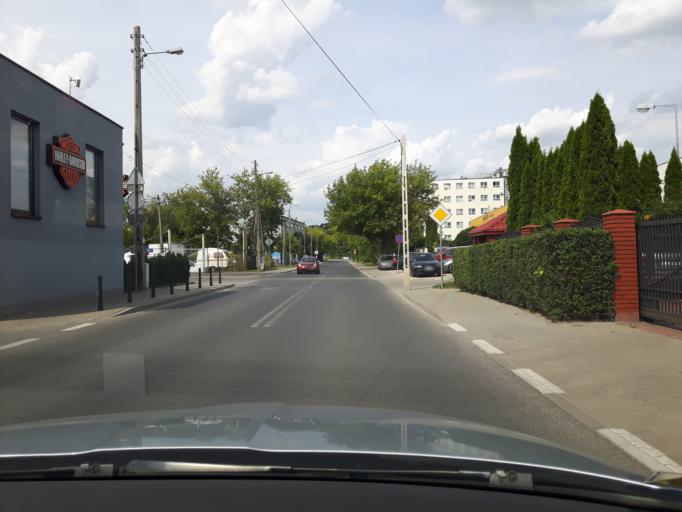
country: PL
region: Masovian Voivodeship
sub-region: Warszawa
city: Ursynow
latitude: 52.1512
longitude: 21.0152
